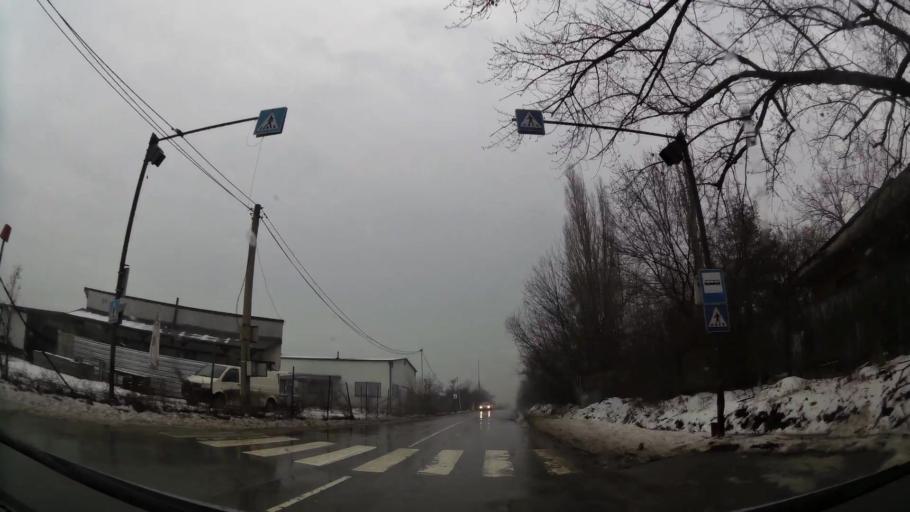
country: BG
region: Sofiya
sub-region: Obshtina Bozhurishte
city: Bozhurishte
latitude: 42.6959
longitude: 23.2397
